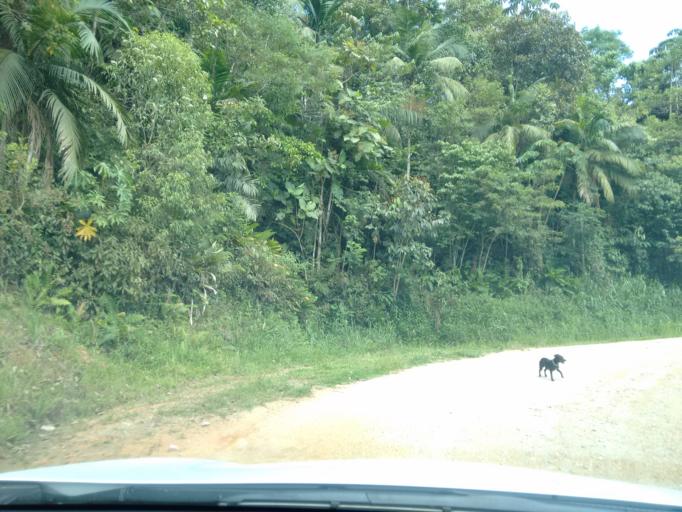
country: BR
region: Santa Catarina
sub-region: Pomerode
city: Pomerode
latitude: -26.7094
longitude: -49.0933
